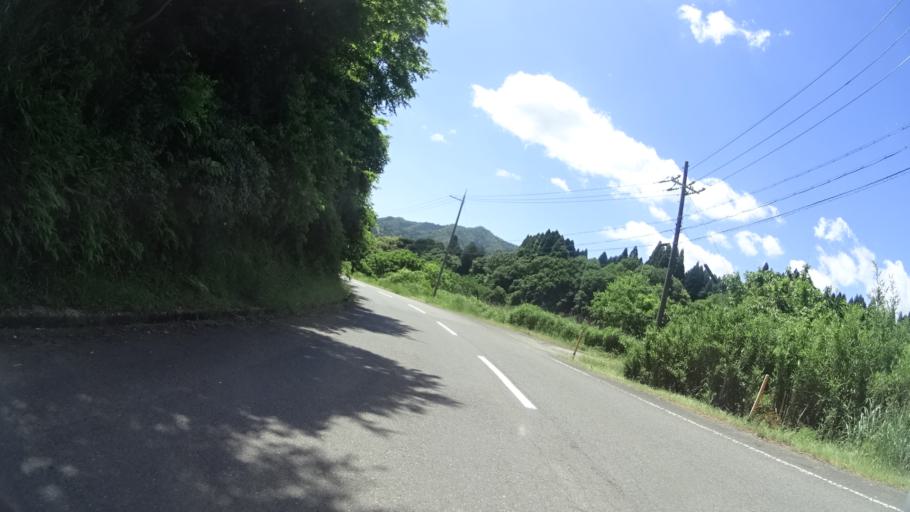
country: JP
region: Kyoto
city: Miyazu
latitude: 35.4178
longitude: 135.1636
